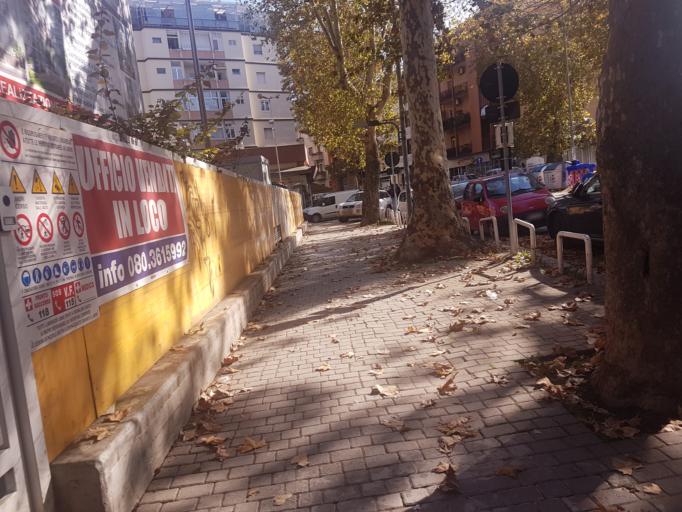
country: IT
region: Apulia
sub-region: Provincia di Bari
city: Bari
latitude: 41.1112
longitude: 16.8648
